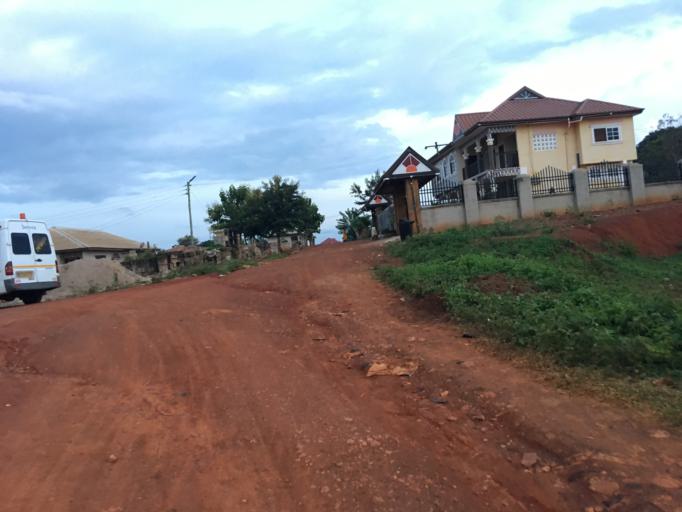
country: GH
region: Western
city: Bibiani
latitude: 6.7868
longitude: -2.5162
